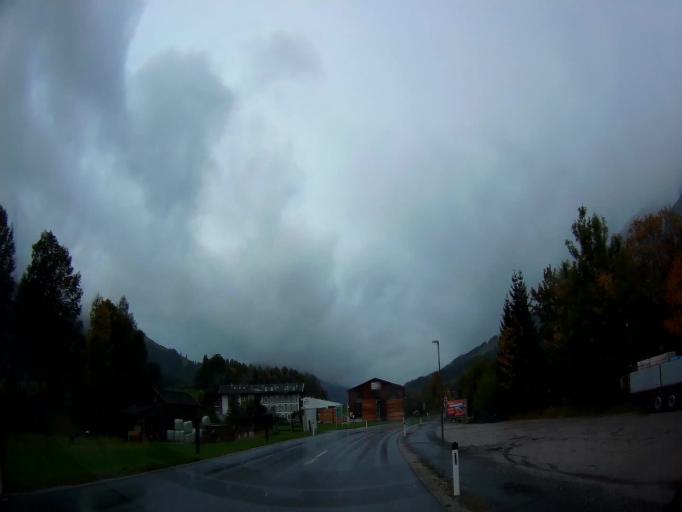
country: AT
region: Salzburg
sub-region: Politischer Bezirk Zell am See
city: Leogang
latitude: 47.4397
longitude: 12.7454
